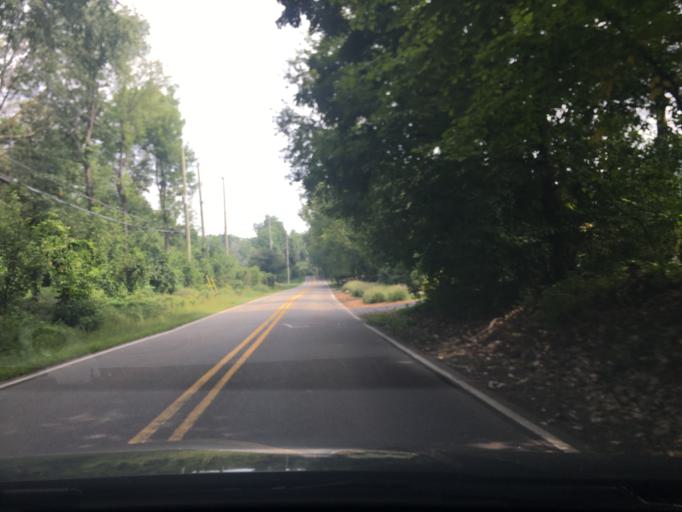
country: US
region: Michigan
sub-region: Oakland County
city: Bloomfield Hills
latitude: 42.5848
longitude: -83.2340
